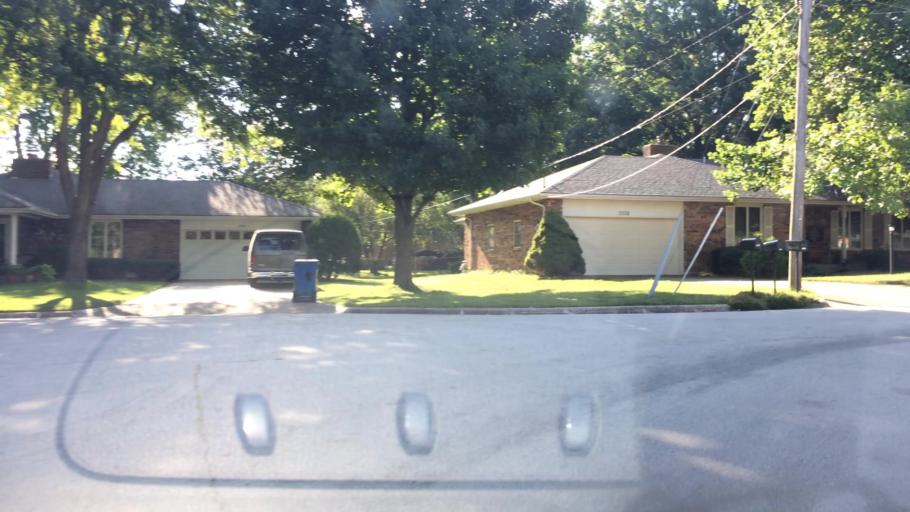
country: US
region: Missouri
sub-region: Greene County
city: Springfield
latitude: 37.2581
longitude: -93.2703
